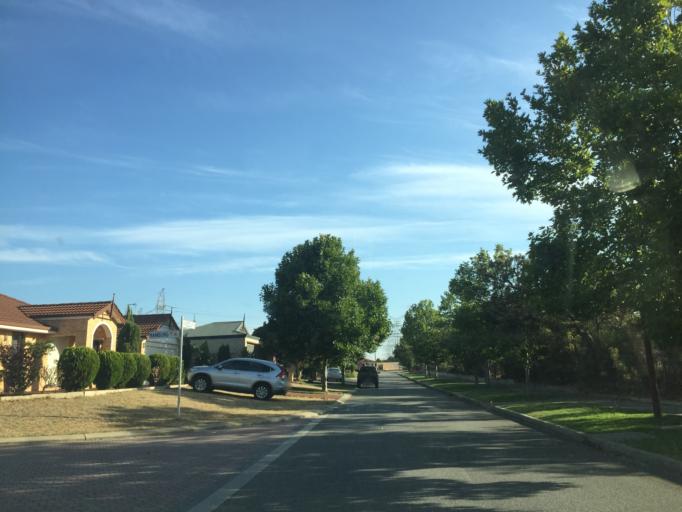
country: AU
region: Western Australia
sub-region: City of Cockburn
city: City of Cockburn
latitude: -32.0934
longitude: 115.8411
